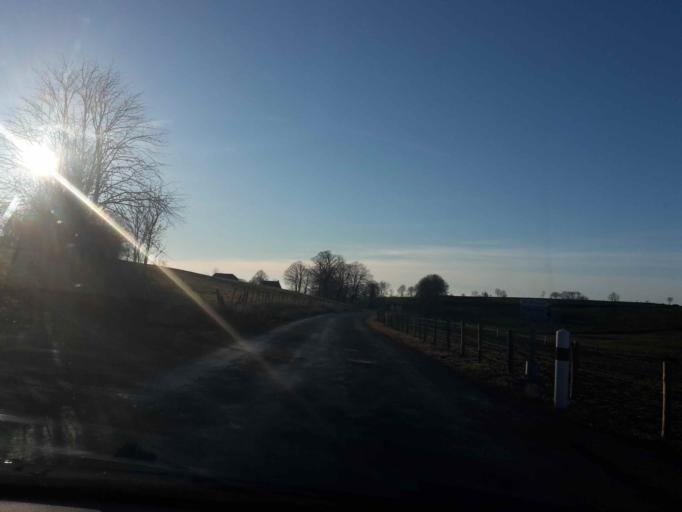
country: FR
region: Auvergne
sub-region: Departement du Cantal
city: Ydes
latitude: 45.2580
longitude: 2.5449
